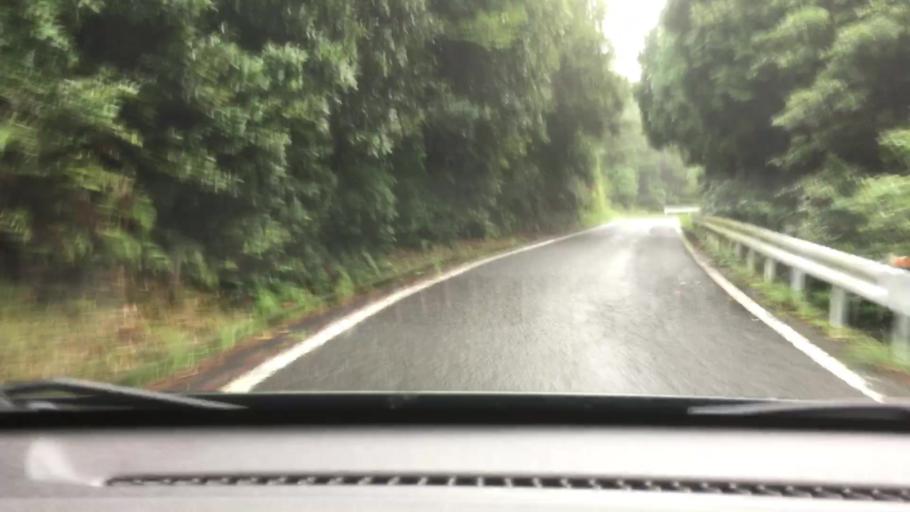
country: JP
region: Nagasaki
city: Togitsu
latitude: 32.9171
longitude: 129.7292
